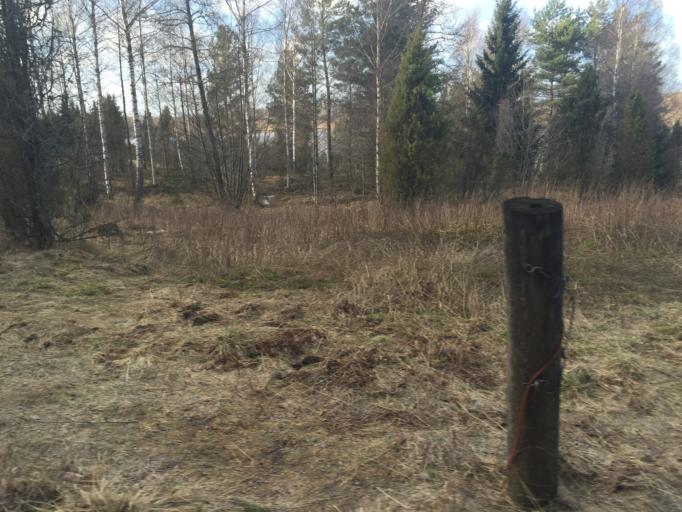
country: SE
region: Soedermanland
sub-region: Vingakers Kommun
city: Vingaker
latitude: 58.9847
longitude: 15.7209
